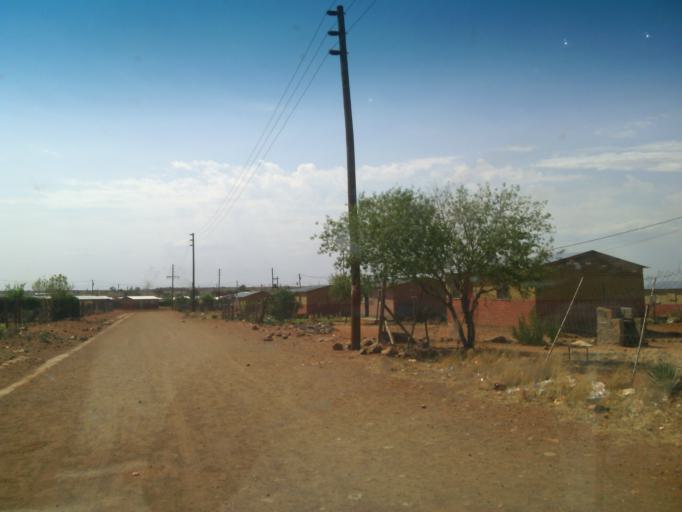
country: ZA
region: Northern Cape
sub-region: Frances Baard District Municipality
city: Barkly West
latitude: -28.5233
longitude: 24.5014
